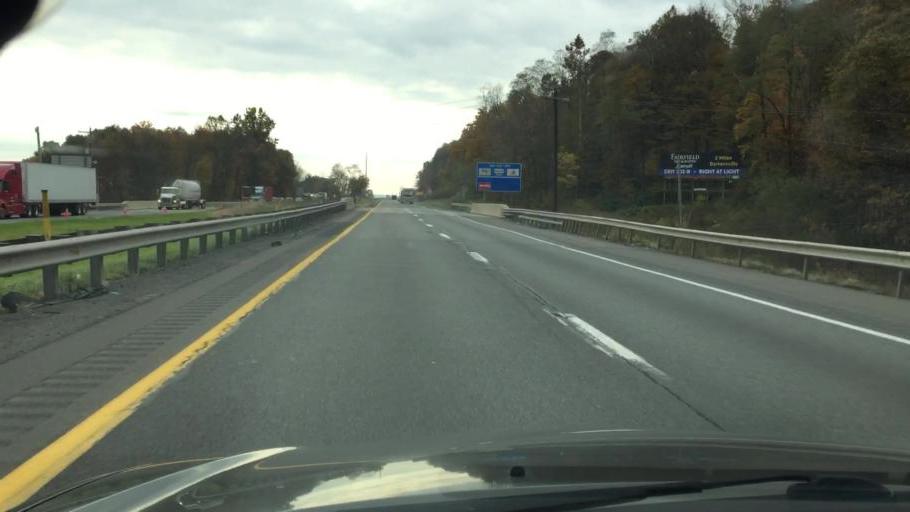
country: US
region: Pennsylvania
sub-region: Monroe County
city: Tannersville
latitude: 41.0481
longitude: -75.3154
